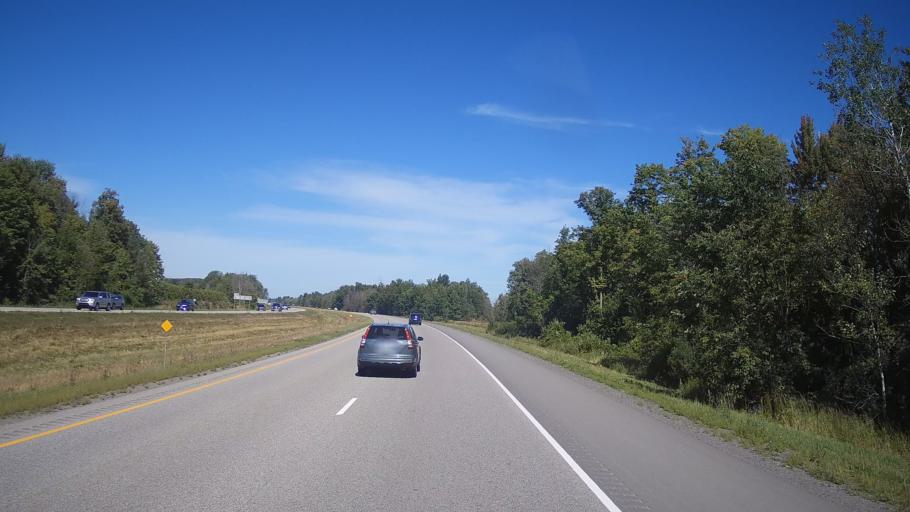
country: CA
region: Ontario
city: Bells Corners
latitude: 45.1611
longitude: -75.6871
